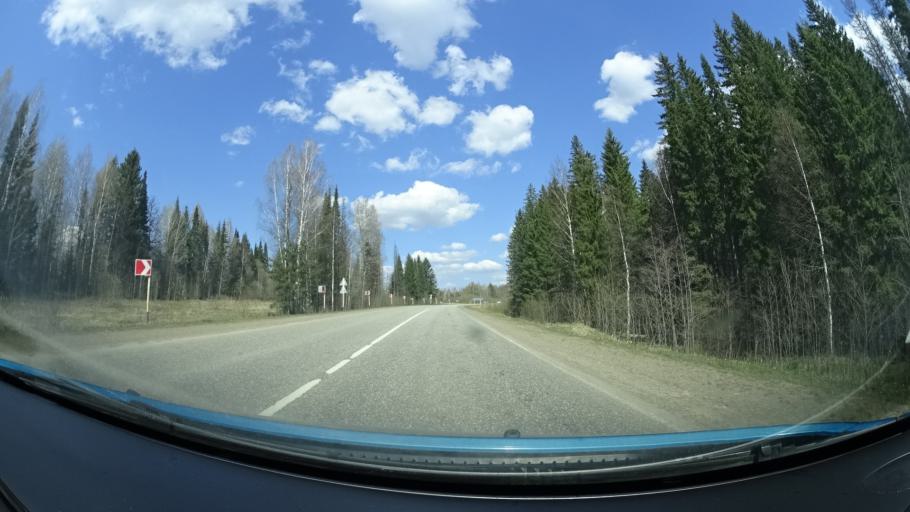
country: RU
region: Perm
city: Osa
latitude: 57.3897
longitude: 55.6087
